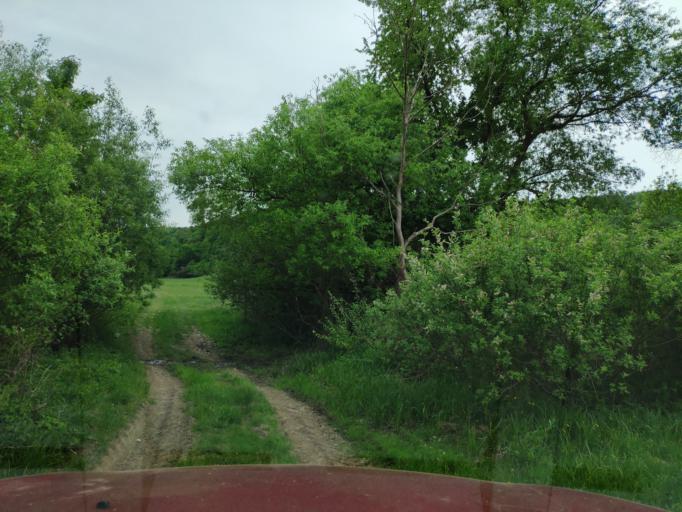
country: SK
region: Banskobystricky
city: Revuca
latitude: 48.5178
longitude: 20.1319
